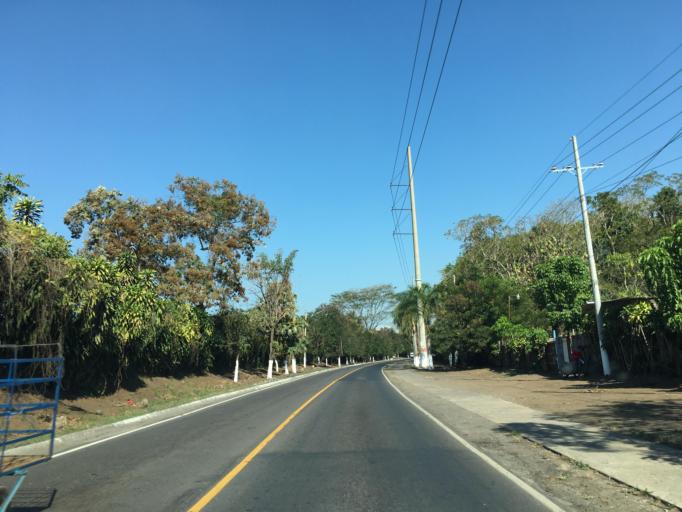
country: GT
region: Escuintla
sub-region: Municipio de La Democracia
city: La Democracia
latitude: 14.2369
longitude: -90.9535
